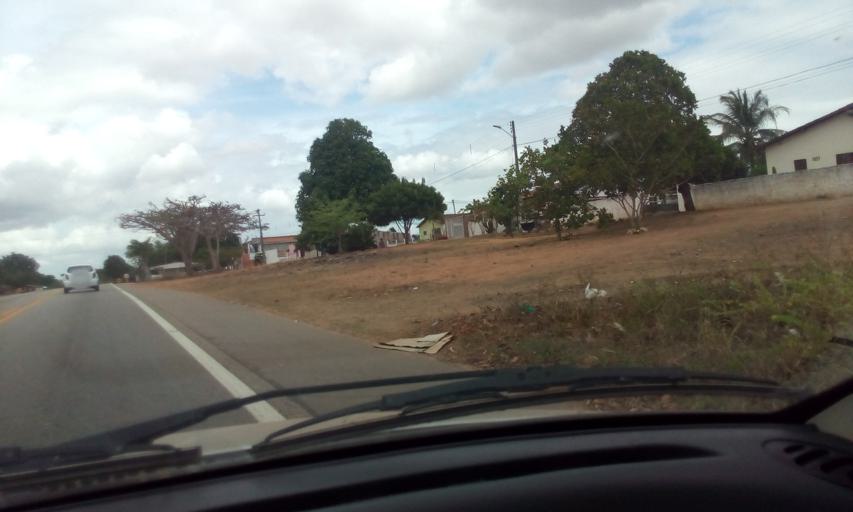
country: BR
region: Rio Grande do Norte
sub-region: Macaiba
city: Macaiba
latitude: -5.9277
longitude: -35.5399
